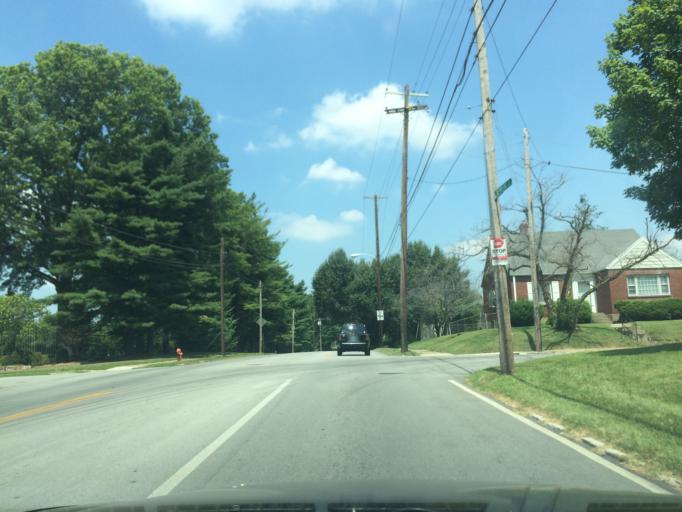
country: US
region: Kentucky
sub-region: Jefferson County
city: Audubon Park
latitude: 38.2258
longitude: -85.7127
